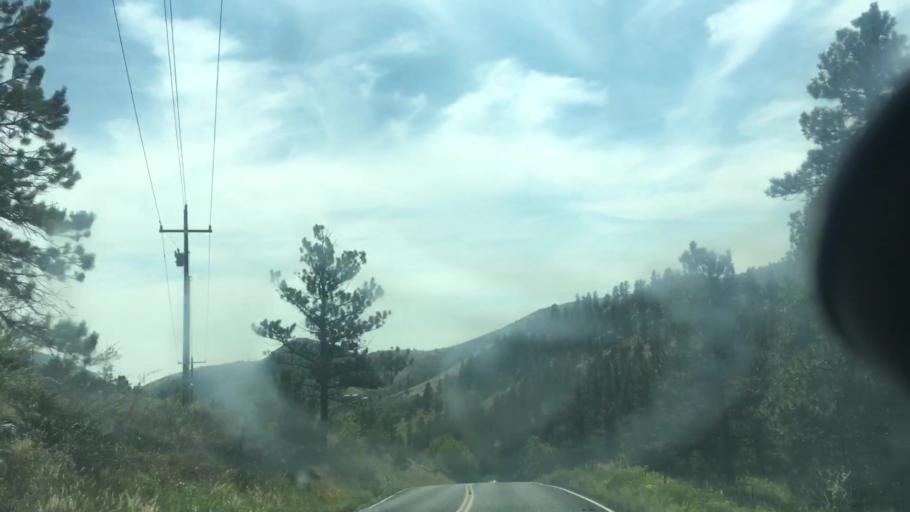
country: US
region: Colorado
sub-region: Larimer County
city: Laporte
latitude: 40.5769
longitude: -105.3289
